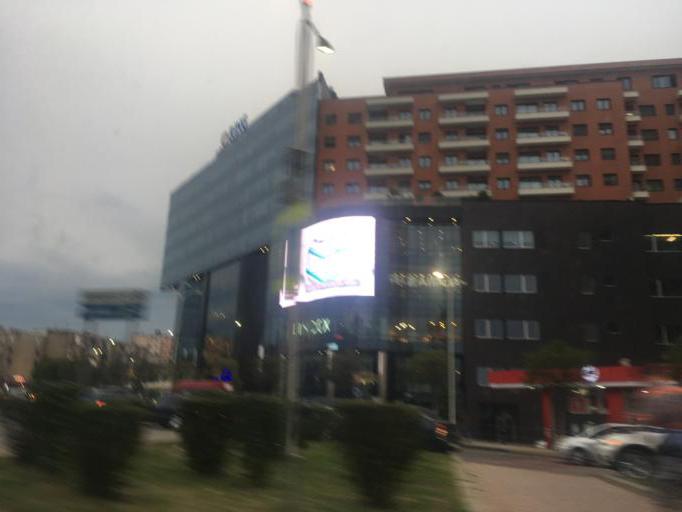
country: AL
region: Tirane
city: Tirana
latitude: 41.3333
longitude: 19.8039
